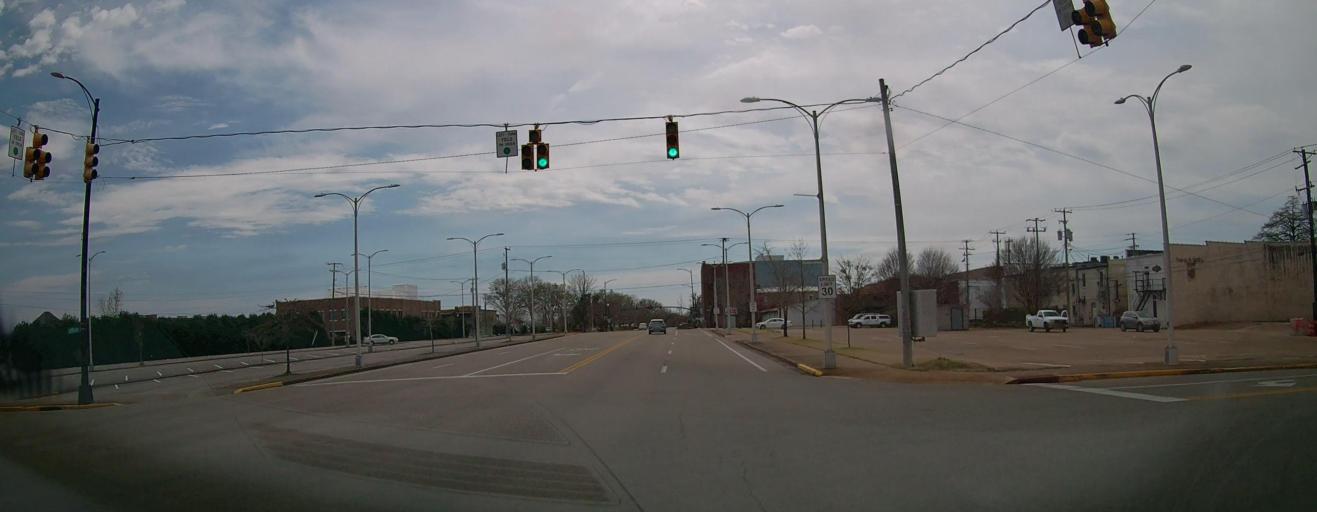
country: US
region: Mississippi
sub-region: Lee County
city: Tupelo
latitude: 34.2593
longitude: -88.7035
